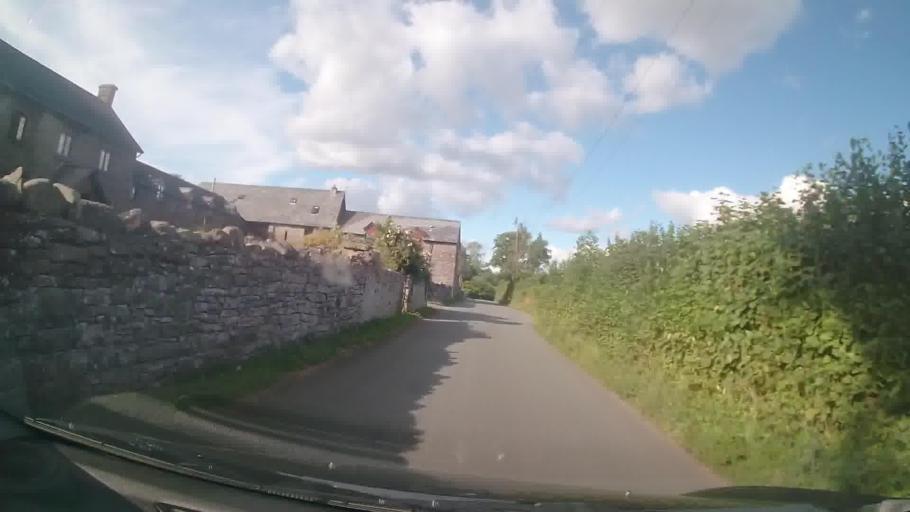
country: GB
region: Wales
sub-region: Sir Powys
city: Brecon
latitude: 51.8860
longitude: -3.3022
